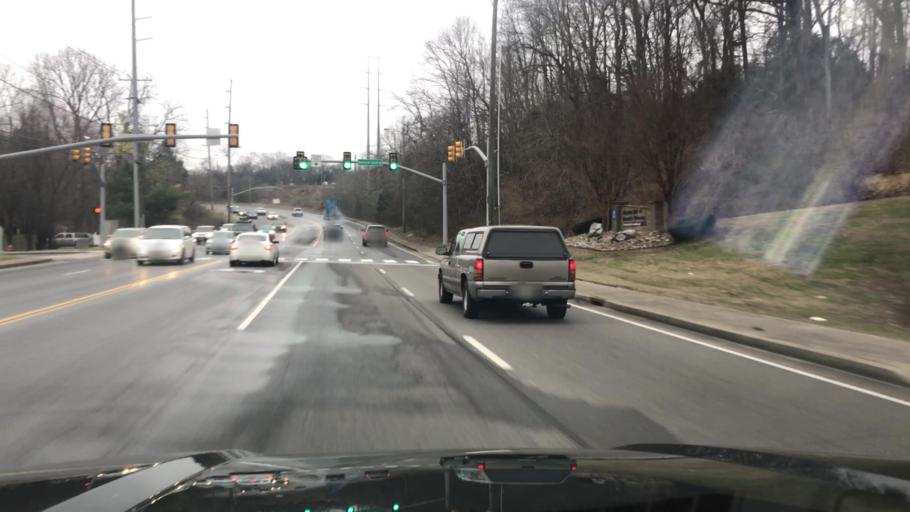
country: US
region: Tennessee
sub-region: Williamson County
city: Brentwood Estates
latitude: 36.0442
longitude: -86.6938
